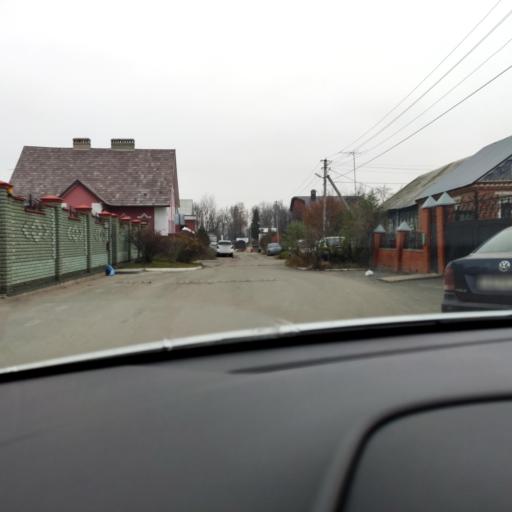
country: RU
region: Tatarstan
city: Vysokaya Gora
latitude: 55.8481
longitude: 49.2158
